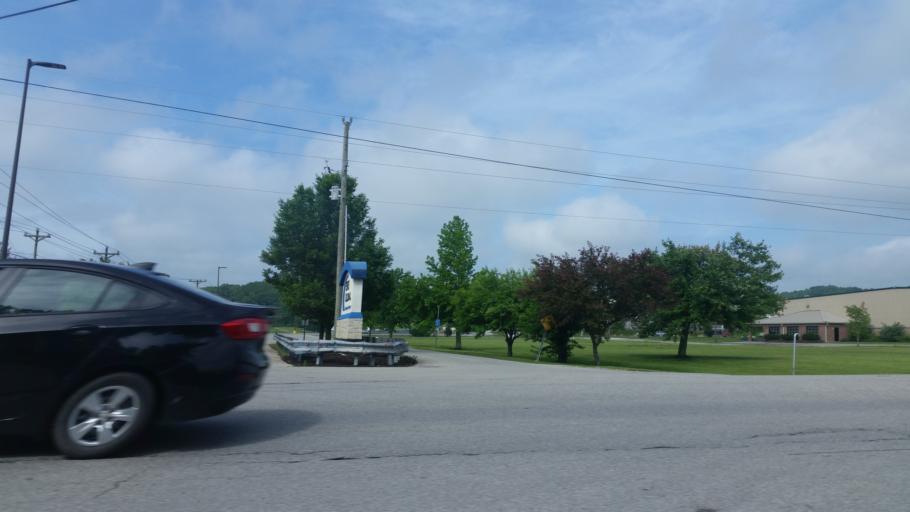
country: US
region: Kentucky
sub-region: Rowan County
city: Morehead
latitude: 38.2106
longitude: -83.4775
